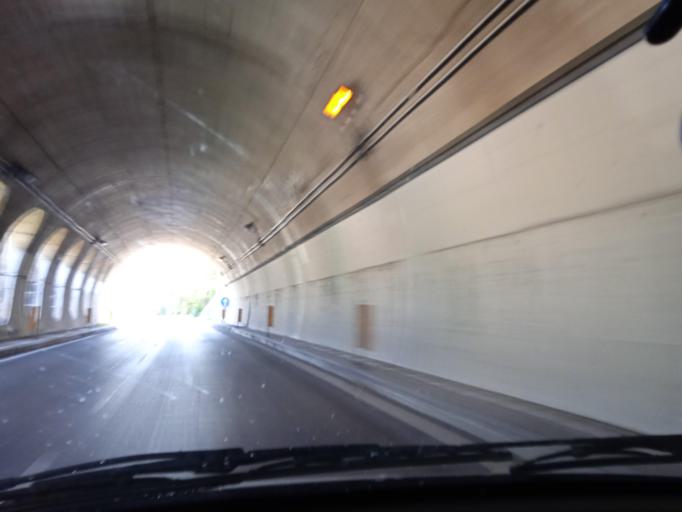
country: IT
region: Sicily
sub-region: Messina
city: Sant'Agata di Militello
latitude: 38.0663
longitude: 14.6517
